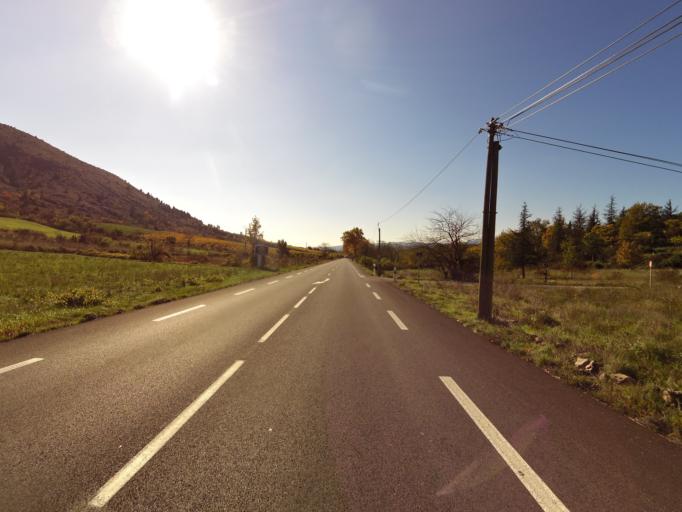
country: FR
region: Rhone-Alpes
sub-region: Departement de l'Ardeche
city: Vesseaux
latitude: 44.6435
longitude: 4.4329
